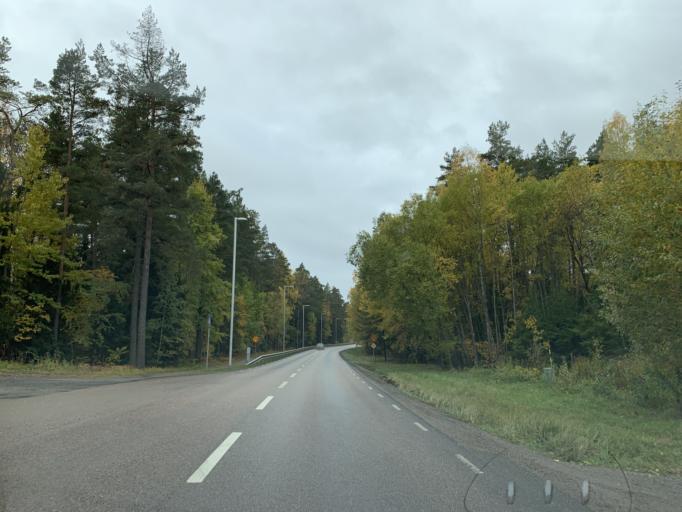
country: SE
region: Stockholm
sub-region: Botkyrka Kommun
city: Varsta
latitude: 59.1786
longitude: 17.8103
